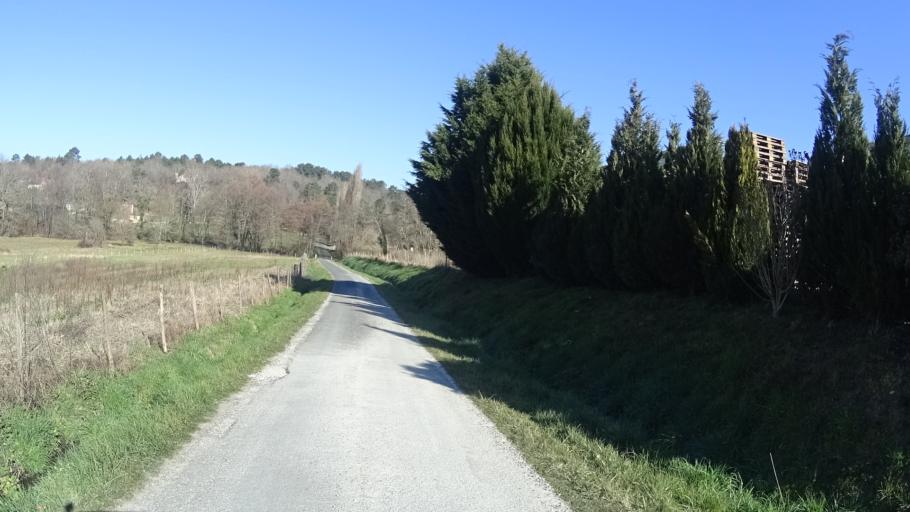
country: FR
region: Aquitaine
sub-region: Departement de la Dordogne
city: Saint-Medard-de-Mussidan
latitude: 45.0402
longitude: 0.2573
